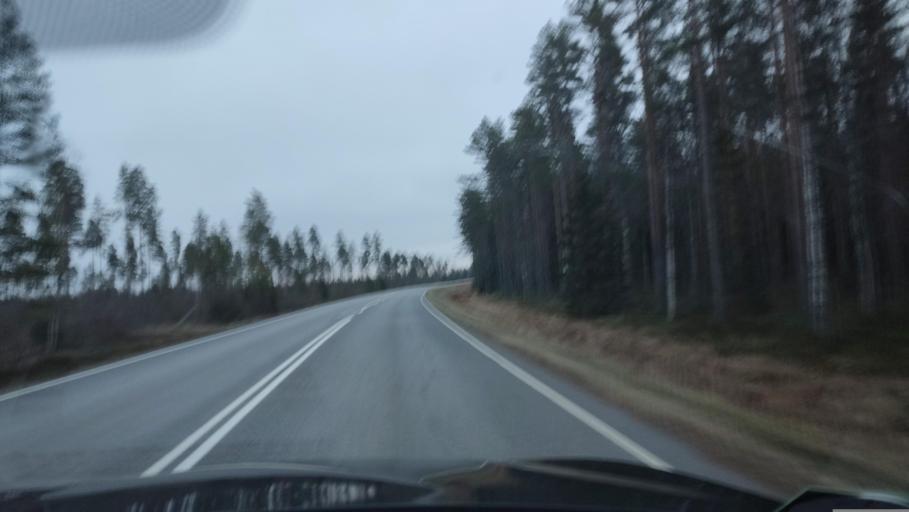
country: FI
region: Southern Ostrobothnia
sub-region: Suupohja
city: Isojoki
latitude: 62.3448
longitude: 21.9670
